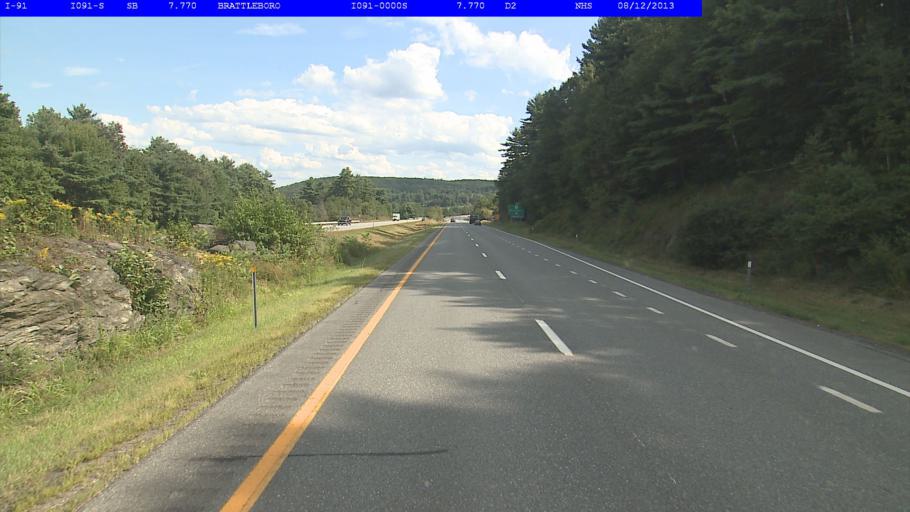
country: US
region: Vermont
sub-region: Windham County
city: Brattleboro
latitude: 42.8391
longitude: -72.5695
